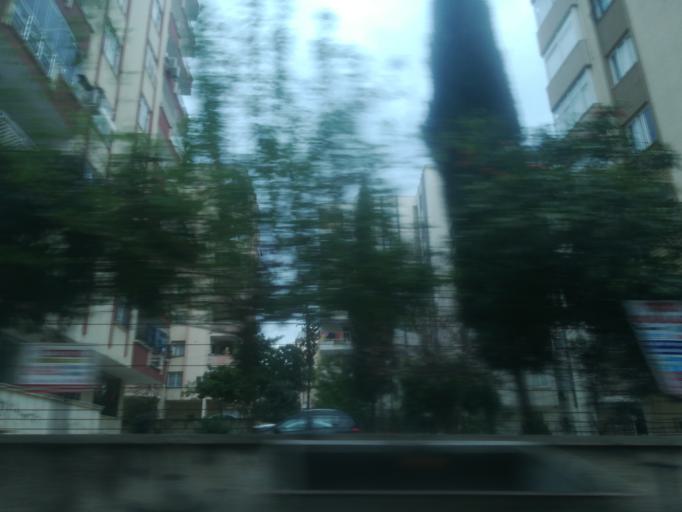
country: TR
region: Adana
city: Adana
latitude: 37.0446
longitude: 35.2897
